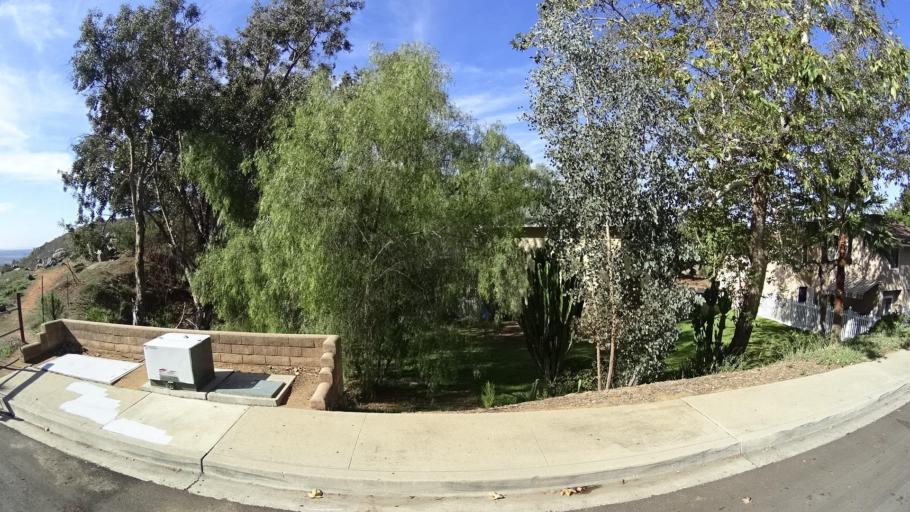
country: US
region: California
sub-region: San Diego County
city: Spring Valley
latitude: 32.7273
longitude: -116.9805
